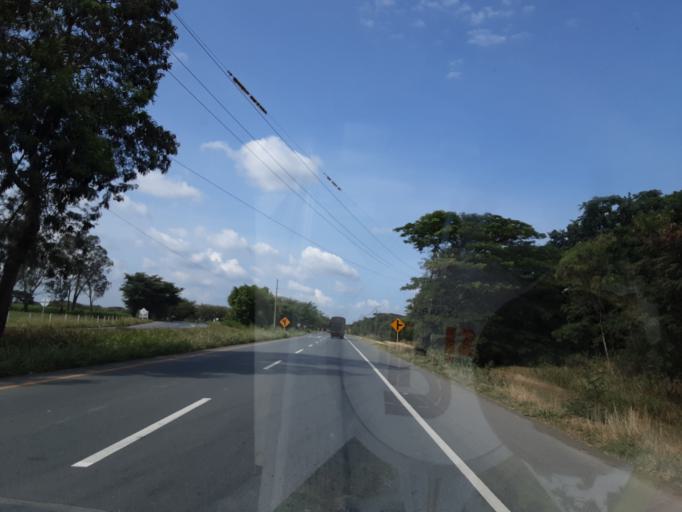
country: CO
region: Valle del Cauca
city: Guacari
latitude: 3.7737
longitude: -76.3265
